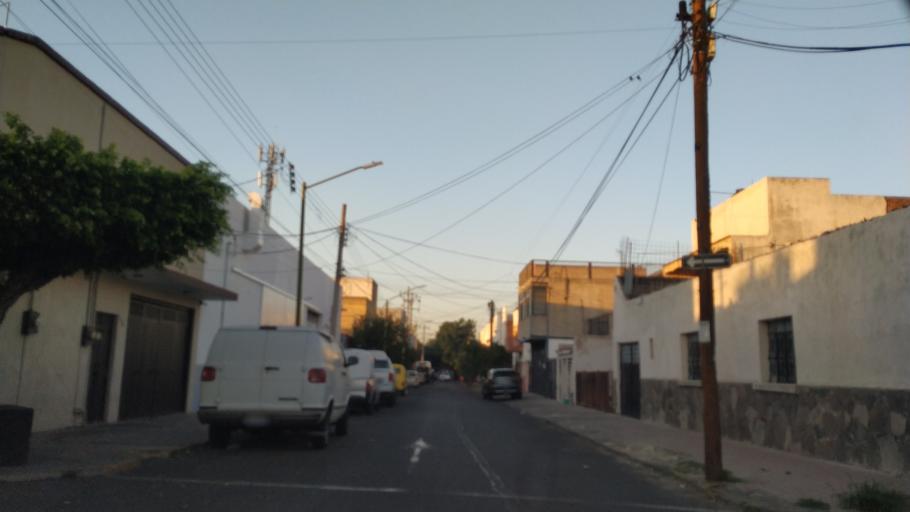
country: MX
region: Jalisco
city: Tlaquepaque
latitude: 20.6568
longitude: -103.3347
